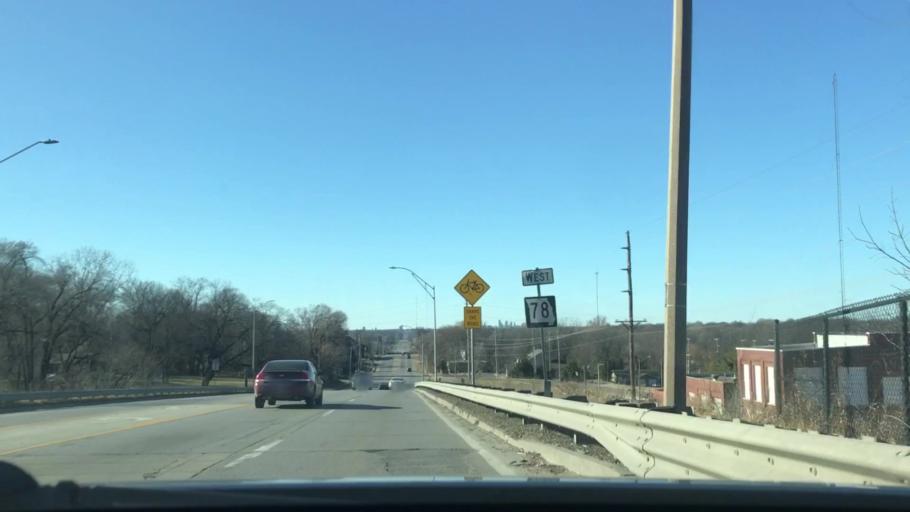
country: US
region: Missouri
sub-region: Jackson County
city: Independence
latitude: 39.0794
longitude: -94.4202
